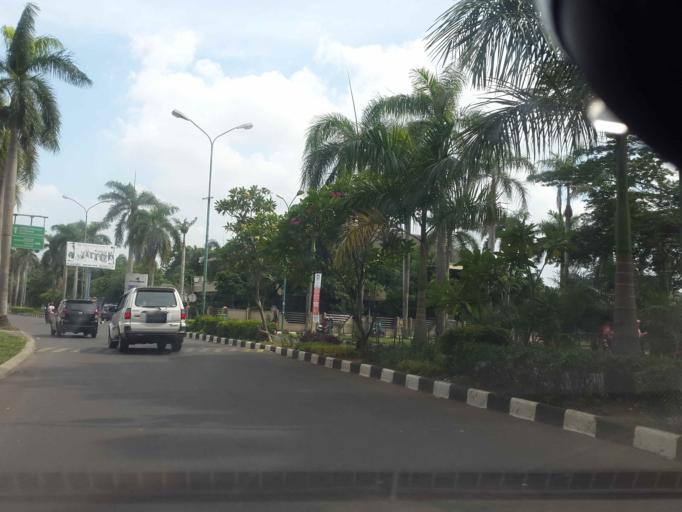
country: ID
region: Banten
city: Tangerang
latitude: -6.1991
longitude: 106.6378
